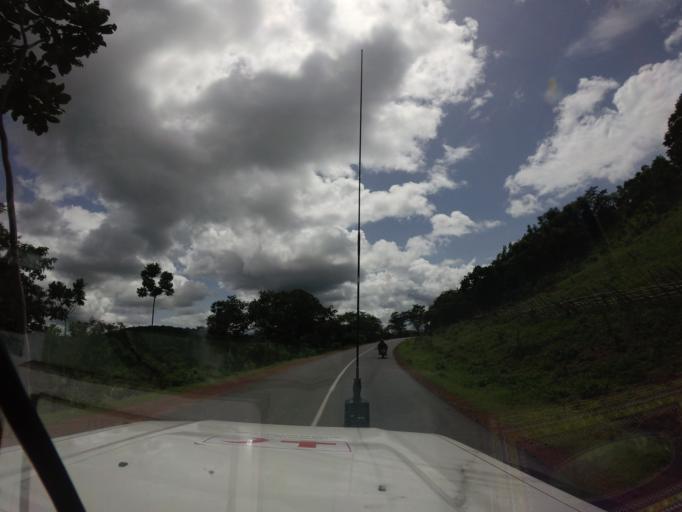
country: SL
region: Northern Province
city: Bindi
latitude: 10.1527
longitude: -11.4863
